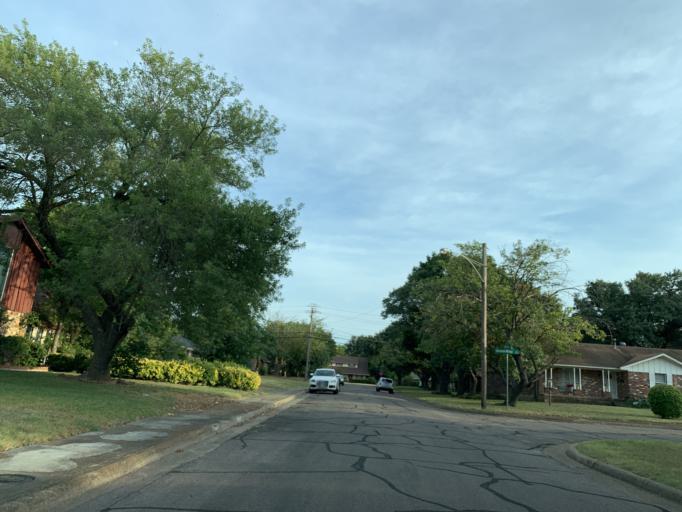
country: US
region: Texas
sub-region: Dallas County
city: Cockrell Hill
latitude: 32.6972
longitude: -96.8819
